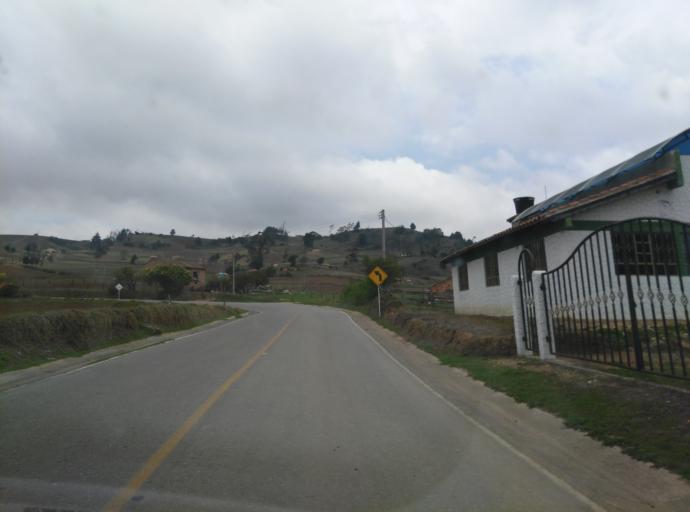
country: CO
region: Boyaca
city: Siachoque
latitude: 5.4968
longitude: -73.2666
